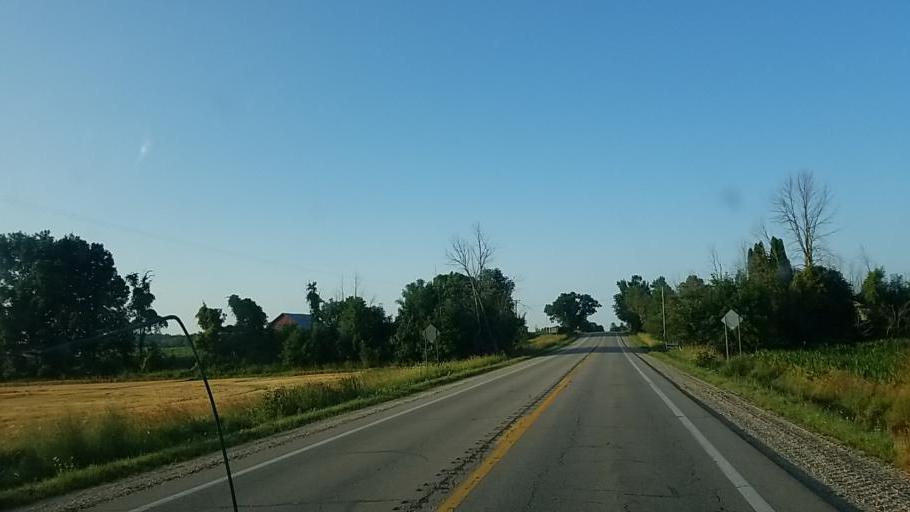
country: US
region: Michigan
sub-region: Montcalm County
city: Lakeview
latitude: 43.4286
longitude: -85.2633
